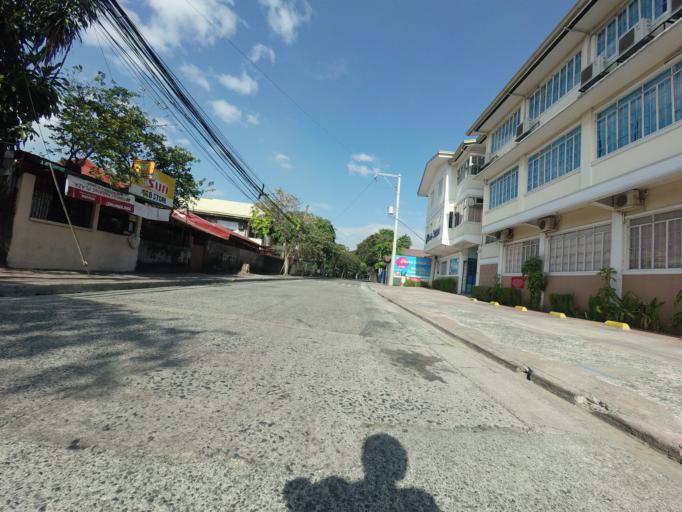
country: PH
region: Calabarzon
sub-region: Province of Rizal
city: Antipolo
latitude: 14.6436
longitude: 121.1139
